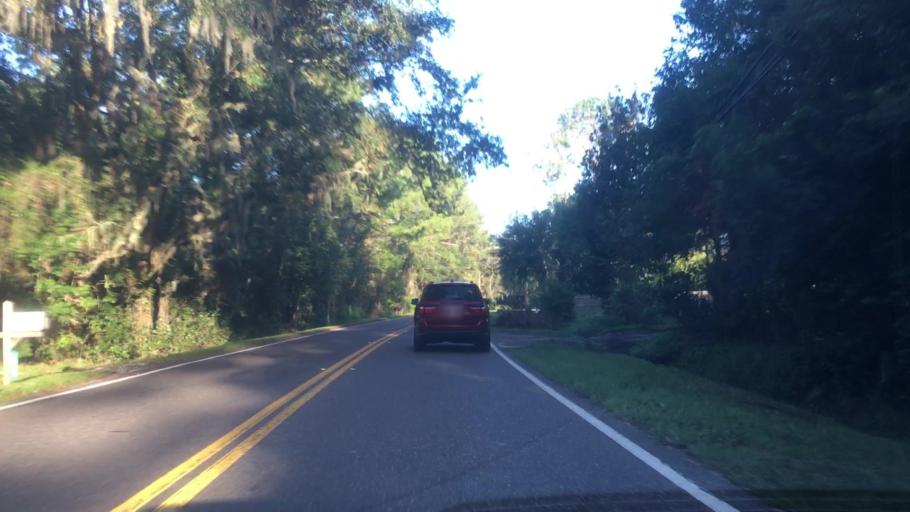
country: US
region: Florida
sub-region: Duval County
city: Jacksonville
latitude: 30.4653
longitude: -81.5957
